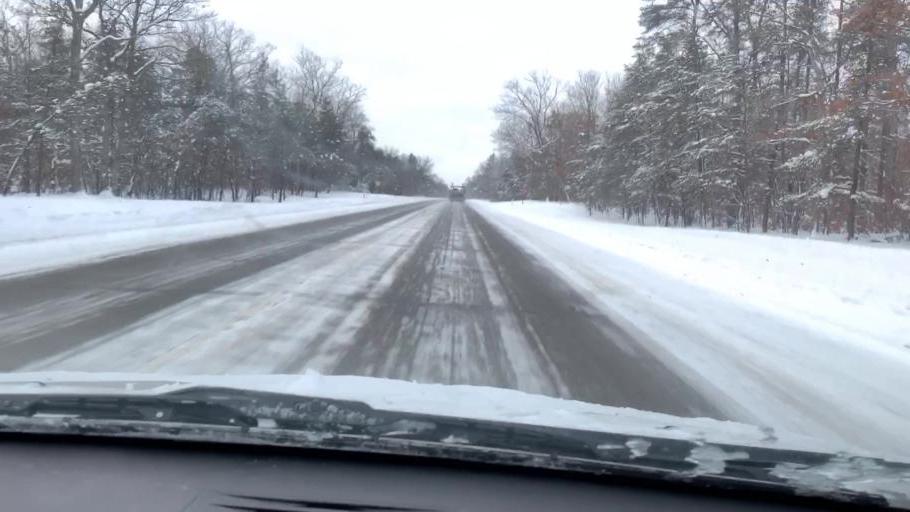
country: US
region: Michigan
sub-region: Wexford County
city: Manton
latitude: 44.5373
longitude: -85.3785
